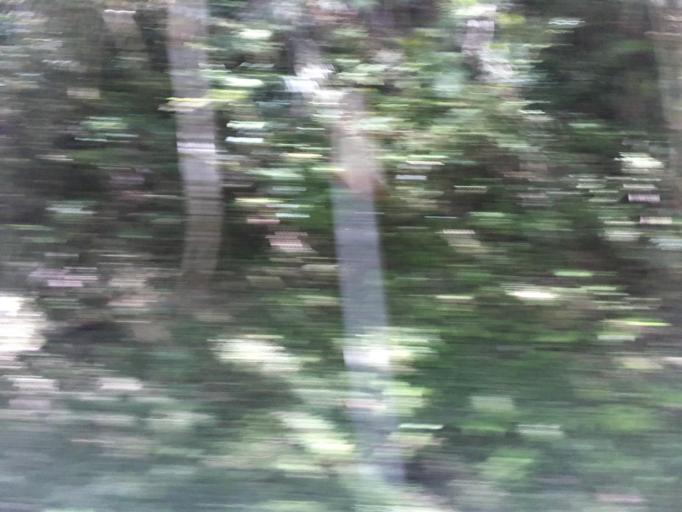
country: TW
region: Taiwan
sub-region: Yilan
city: Yilan
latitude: 24.5335
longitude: 121.5208
